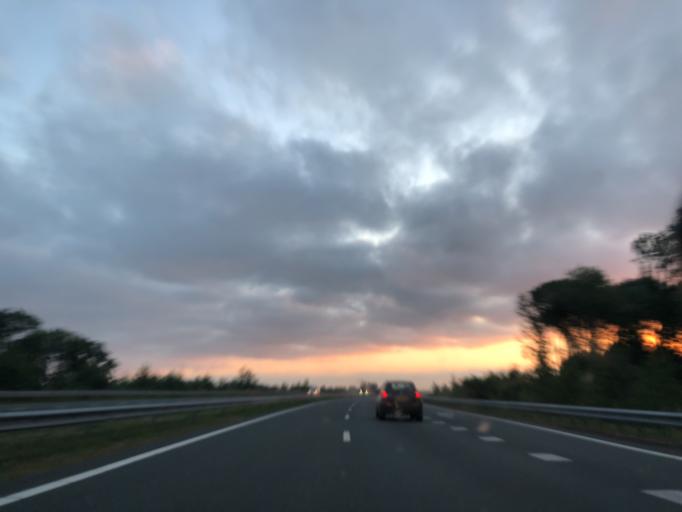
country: NL
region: Groningen
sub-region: Gemeente Veendam
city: Veendam
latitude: 53.0938
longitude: 6.8923
